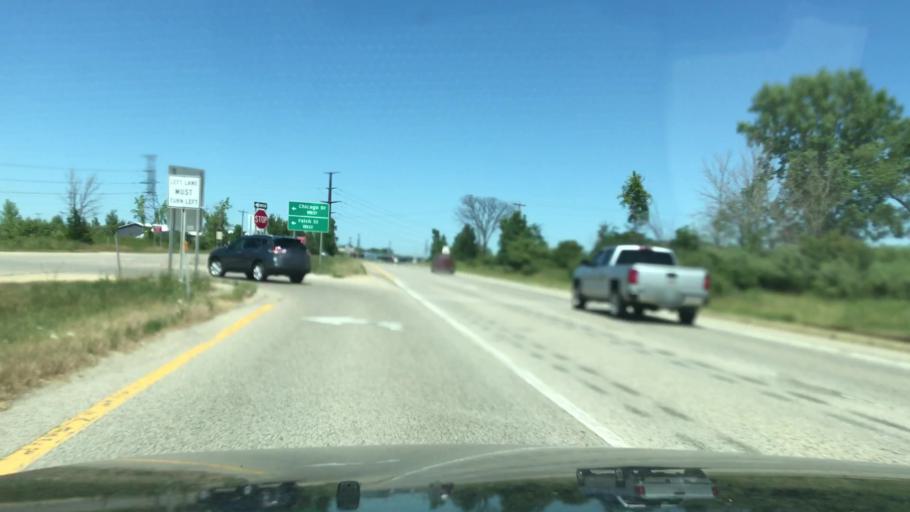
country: US
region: Michigan
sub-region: Ottawa County
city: Zeeland
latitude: 42.8208
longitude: -85.9860
